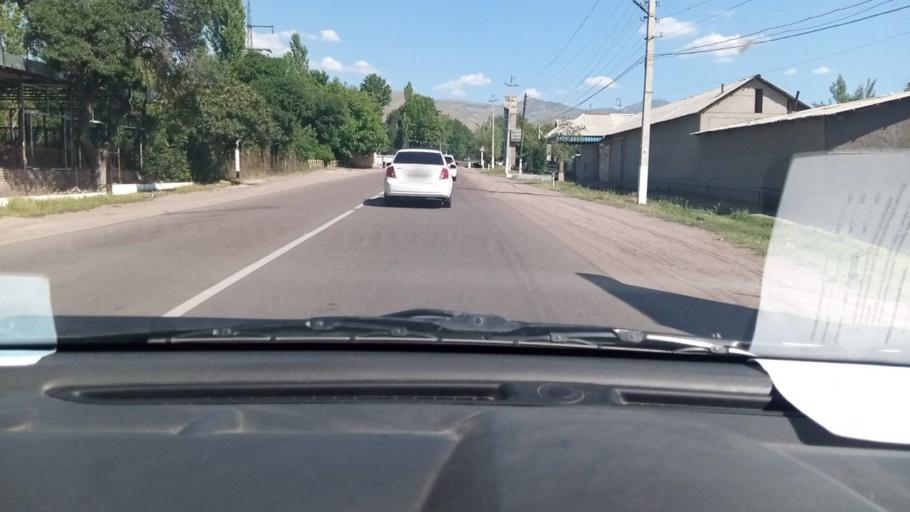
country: UZ
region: Toshkent
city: Angren
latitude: 41.0390
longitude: 70.0943
